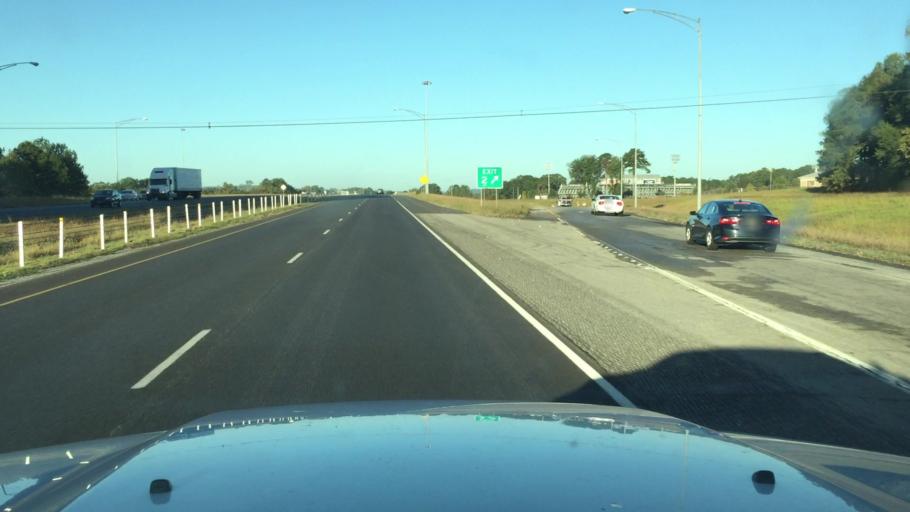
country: US
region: Alabama
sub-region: Etowah County
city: Gadsden
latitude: 33.9920
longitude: -86.0334
